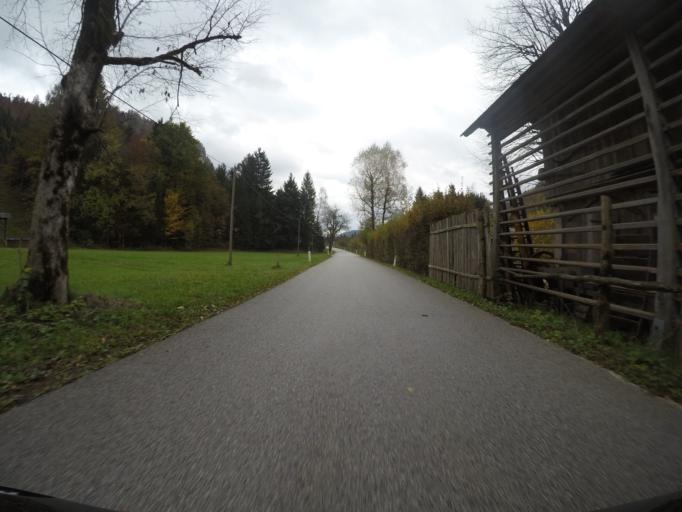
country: SI
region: Gorje
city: Zgornje Gorje
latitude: 46.3848
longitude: 14.0388
